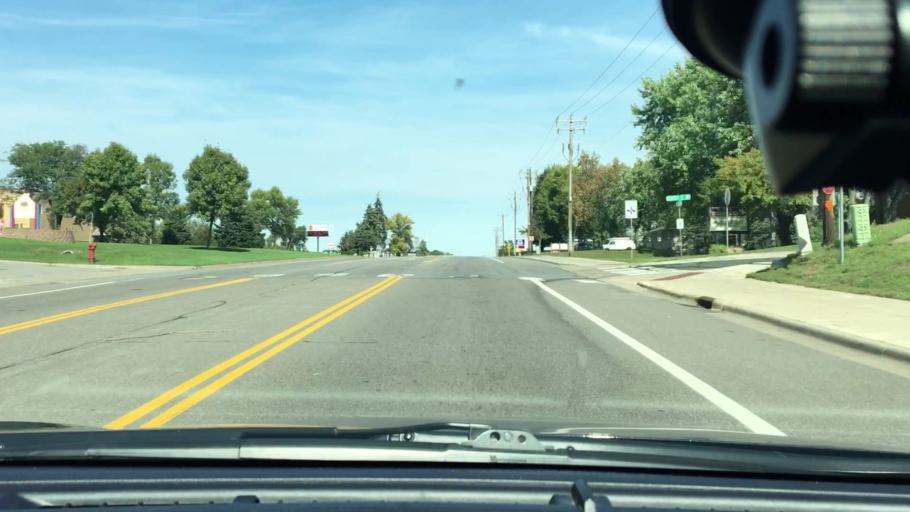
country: US
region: Minnesota
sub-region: Wright County
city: Hanover
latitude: 45.1558
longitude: -93.6660
